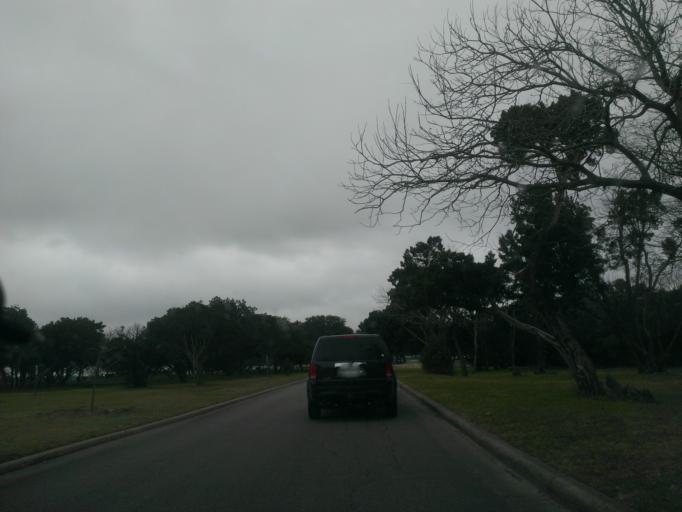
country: US
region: Texas
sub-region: Travis County
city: Wells Branch
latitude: 30.4025
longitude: -97.6856
